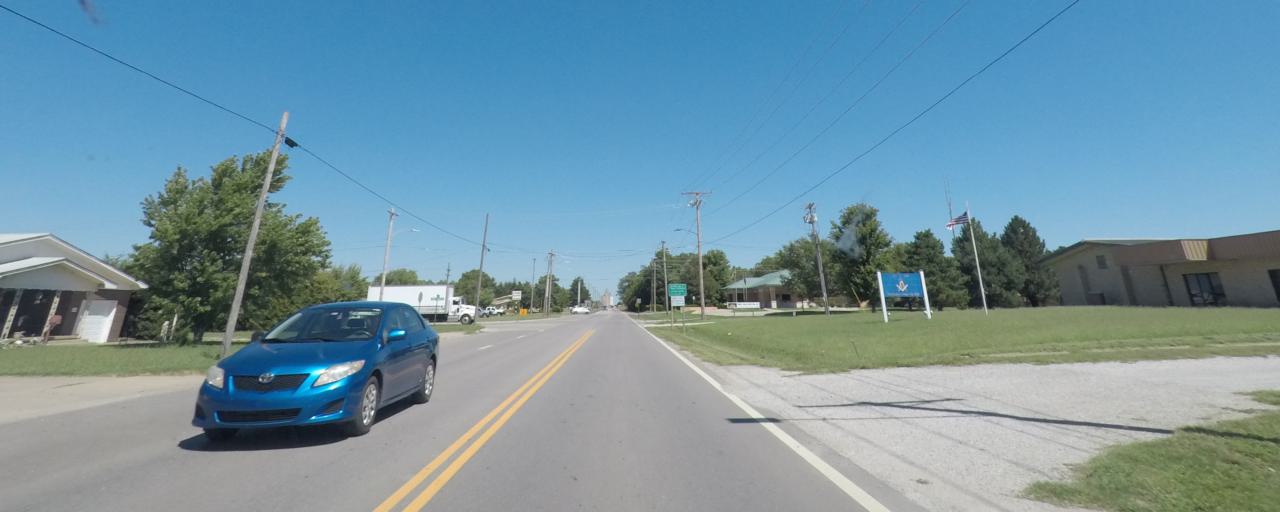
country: US
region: Kansas
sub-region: Sumner County
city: Wellington
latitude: 37.2881
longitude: -97.3943
